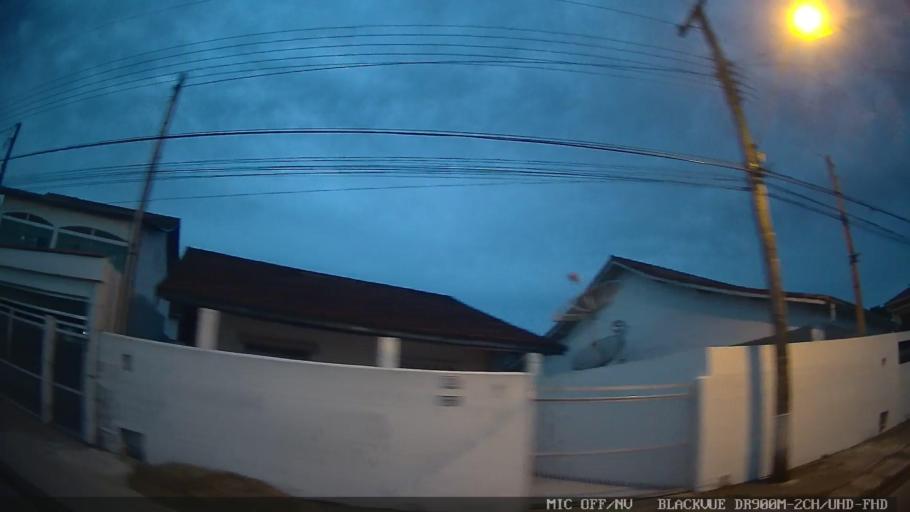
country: BR
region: Sao Paulo
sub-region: Iguape
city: Iguape
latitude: -24.7429
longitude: -47.5472
